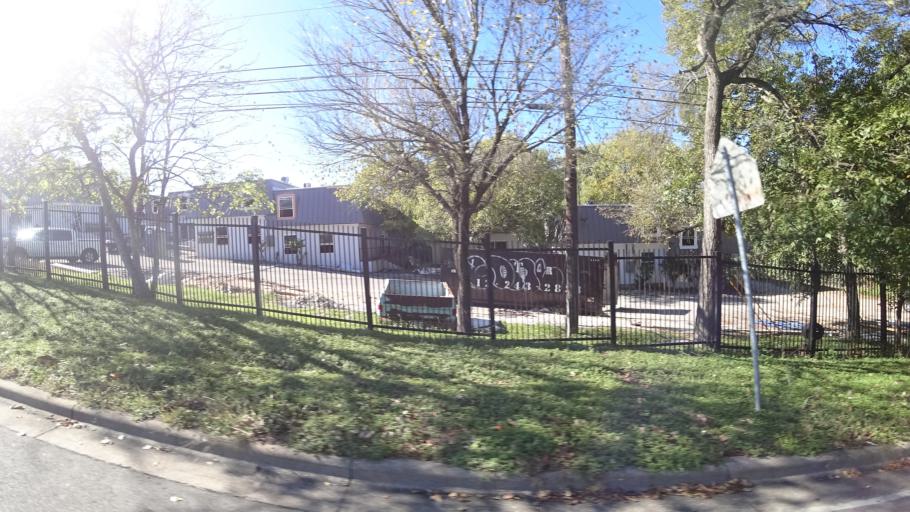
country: US
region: Texas
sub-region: Travis County
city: Austin
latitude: 30.2985
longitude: -97.6878
